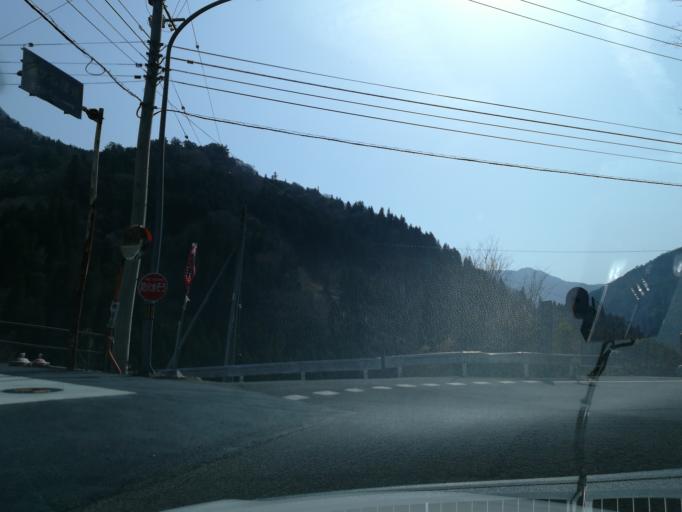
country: JP
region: Tokushima
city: Ikedacho
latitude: 33.8715
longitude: 133.9155
